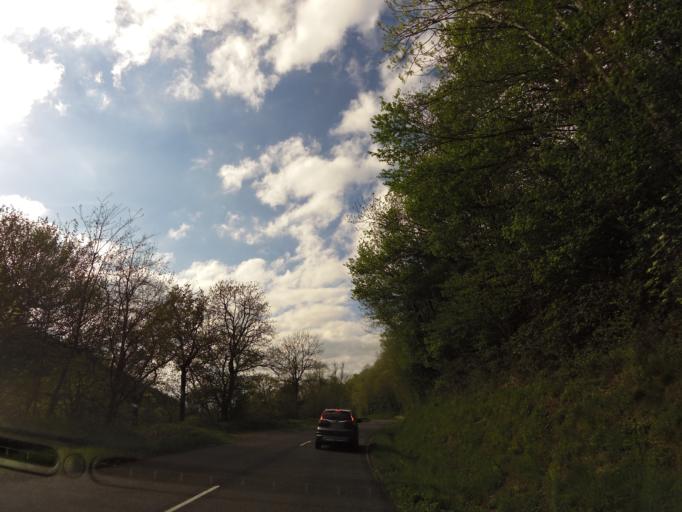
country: FR
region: Midi-Pyrenees
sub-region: Departement du Tarn
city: Soreze
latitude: 43.4280
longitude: 2.0564
